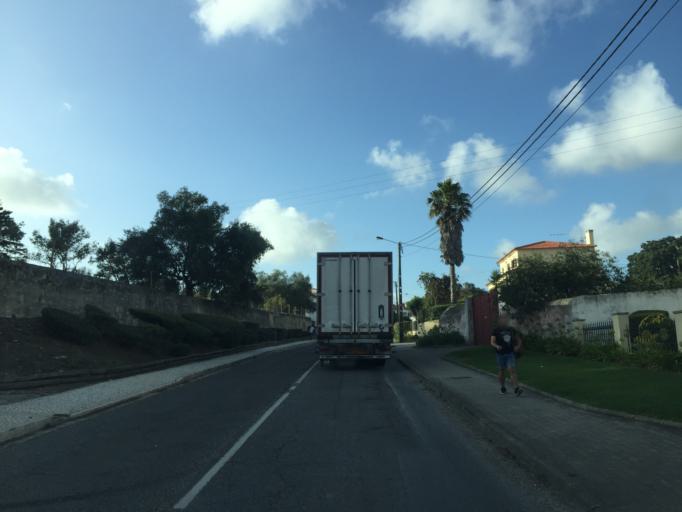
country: PT
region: Lisbon
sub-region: Torres Vedras
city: Torres Vedras
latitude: 39.1027
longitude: -9.2591
